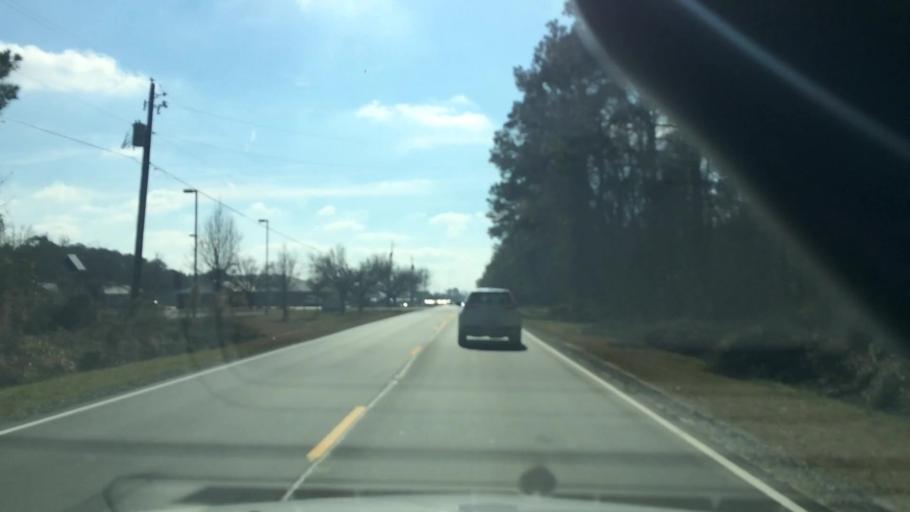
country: US
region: North Carolina
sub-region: Duplin County
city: Beulaville
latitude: 34.9323
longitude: -77.7715
